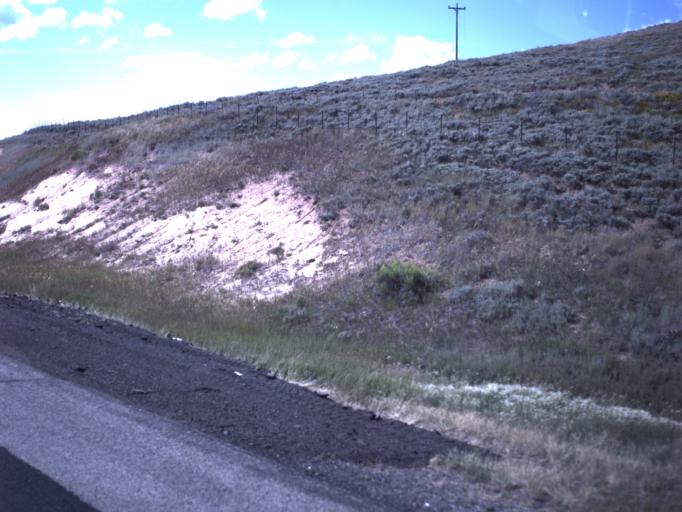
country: US
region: Utah
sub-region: Wasatch County
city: Heber
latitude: 40.1977
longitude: -111.1018
